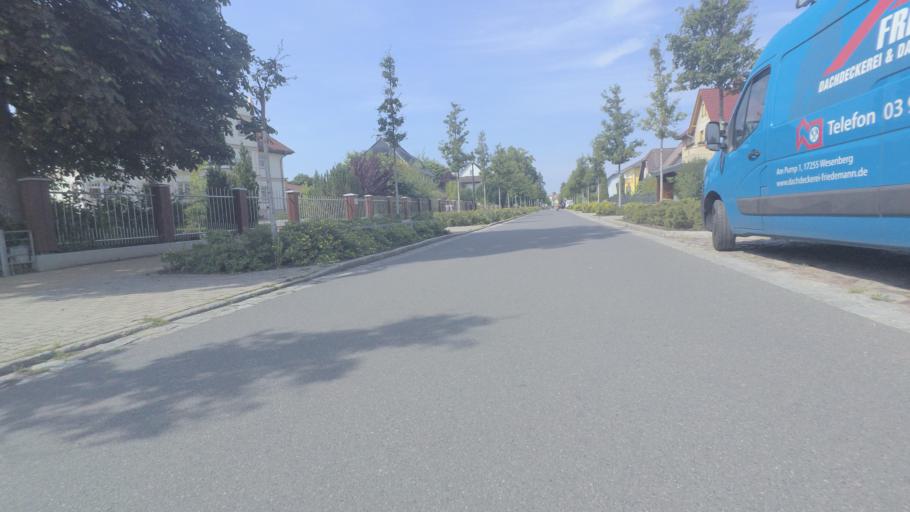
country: DE
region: Mecklenburg-Vorpommern
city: Waren
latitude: 53.5160
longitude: 12.6733
